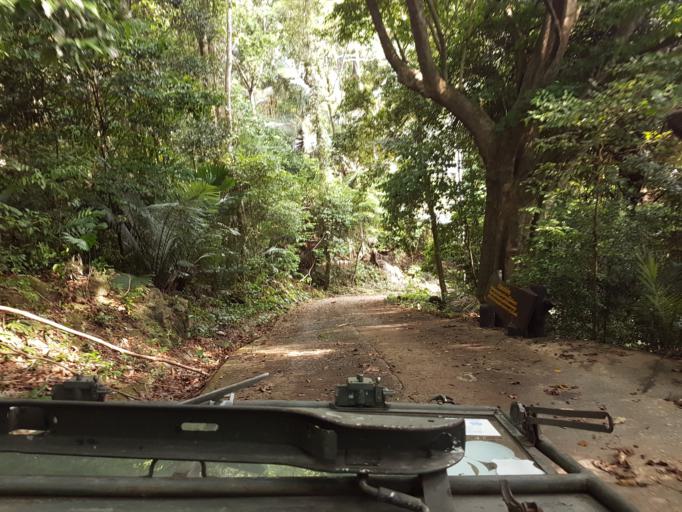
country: TH
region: Pattani
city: Khok Pho
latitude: 6.6559
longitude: 101.1004
